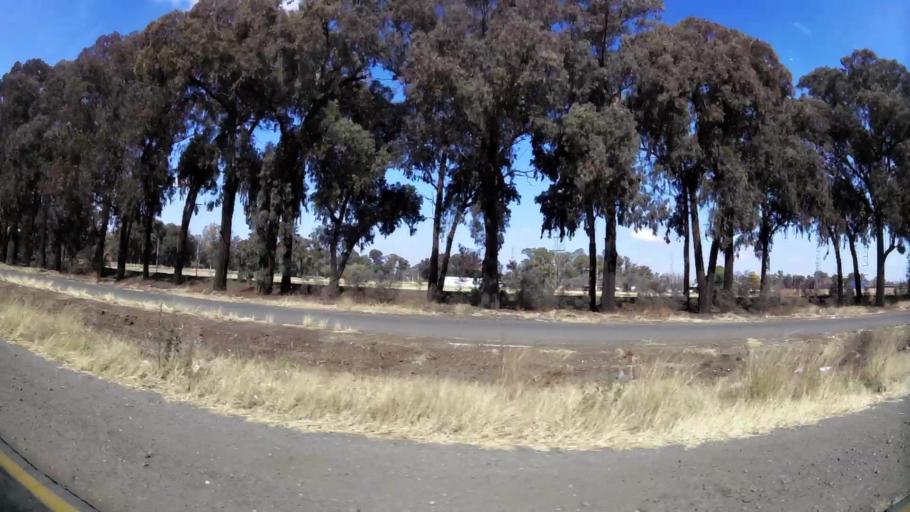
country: ZA
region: Orange Free State
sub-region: Mangaung Metropolitan Municipality
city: Bloemfontein
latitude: -29.1163
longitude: 26.2438
